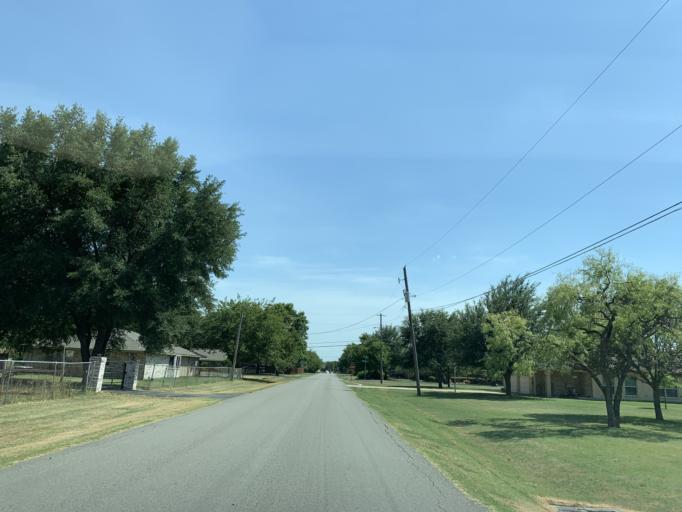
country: US
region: Texas
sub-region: Dallas County
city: Cedar Hill
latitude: 32.6497
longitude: -97.0210
